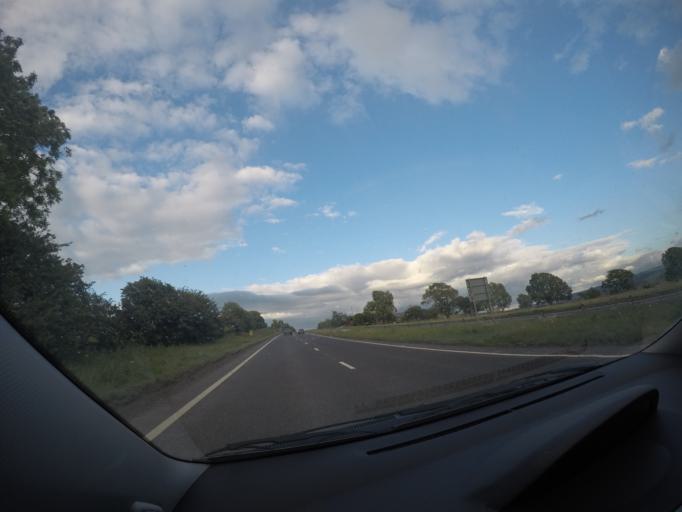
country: GB
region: England
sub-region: County Durham
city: Lartington
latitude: 54.5185
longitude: -1.9759
